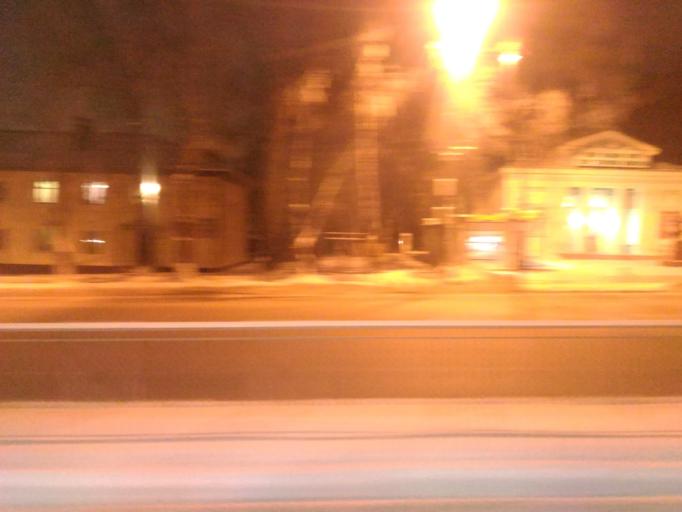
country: RU
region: Ulyanovsk
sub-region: Ulyanovskiy Rayon
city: Ulyanovsk
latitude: 54.3405
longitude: 48.3788
